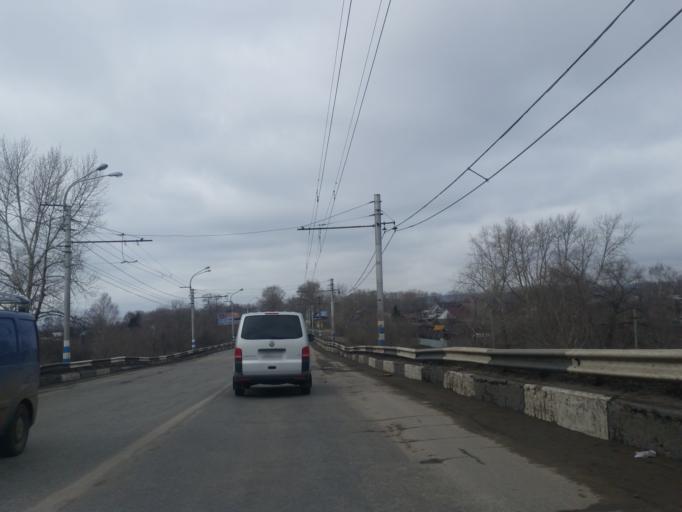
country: RU
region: Ulyanovsk
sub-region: Ulyanovskiy Rayon
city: Ulyanovsk
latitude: 54.3318
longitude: 48.5051
